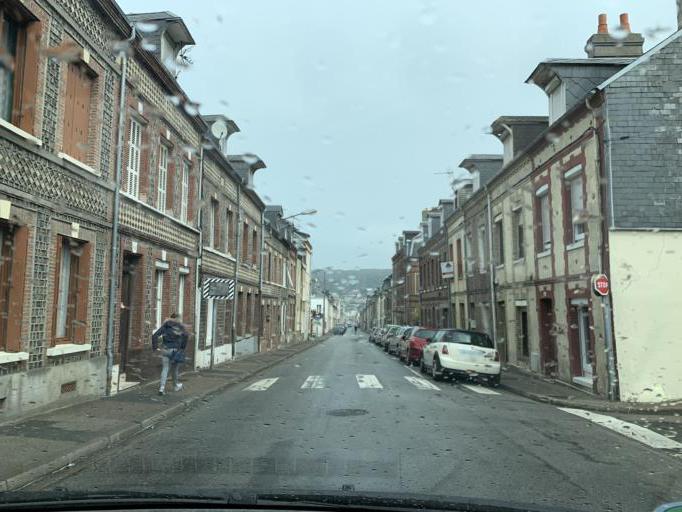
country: FR
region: Haute-Normandie
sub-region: Departement de la Seine-Maritime
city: Fecamp
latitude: 49.7572
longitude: 0.3630
